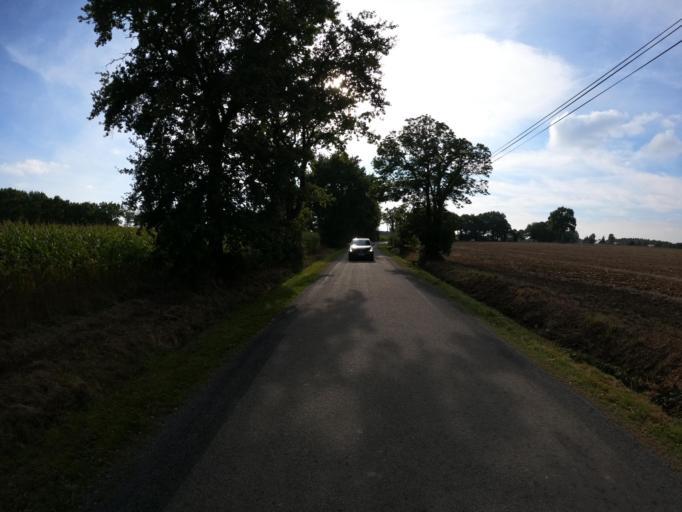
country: FR
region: Brittany
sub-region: Departement du Morbihan
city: Ploermel
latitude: 47.8718
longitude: -2.4075
